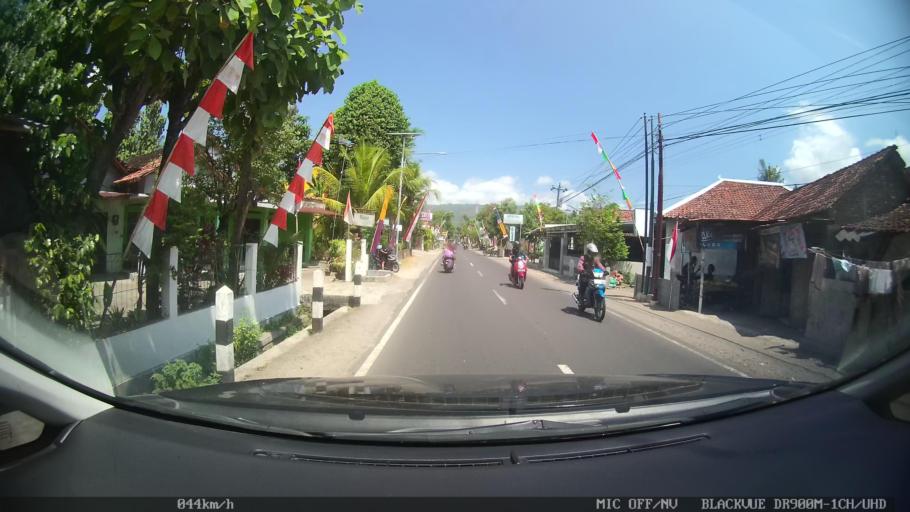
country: ID
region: Daerah Istimewa Yogyakarta
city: Pundong
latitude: -7.9367
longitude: 110.3739
